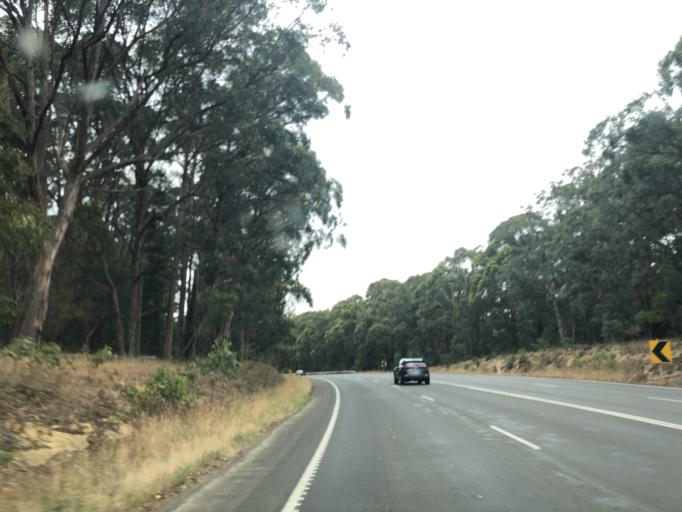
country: AU
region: Victoria
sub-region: Hume
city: Sunbury
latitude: -37.3984
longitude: 144.5290
